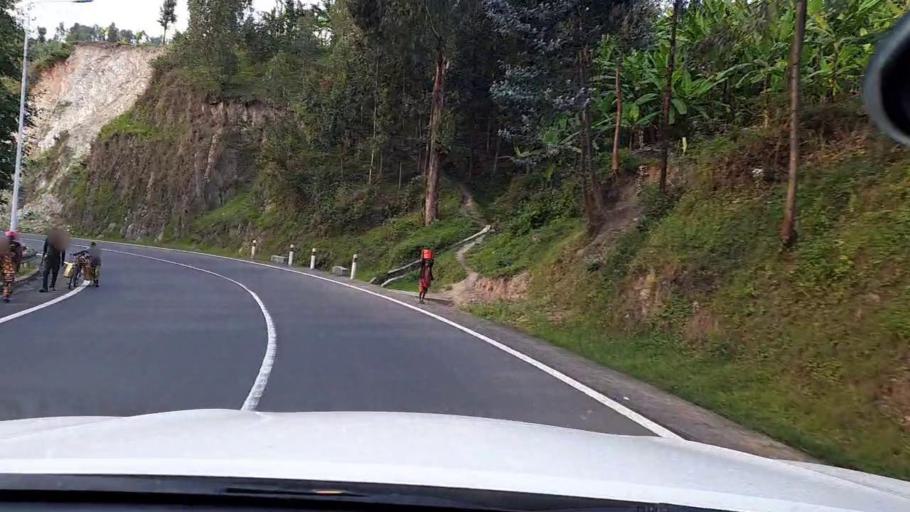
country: RW
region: Western Province
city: Kibuye
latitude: -2.0845
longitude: 29.4093
